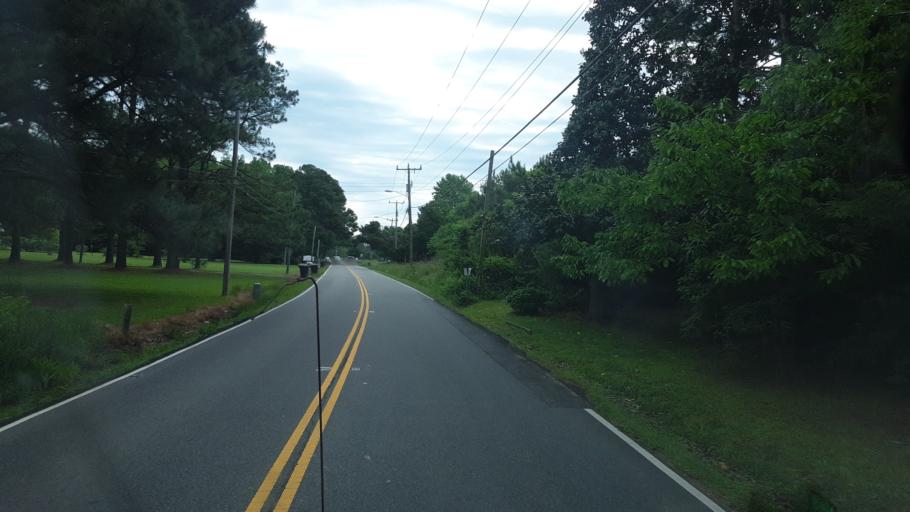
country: US
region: Virginia
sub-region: City of Virginia Beach
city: Virginia Beach
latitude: 36.7306
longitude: -75.9812
